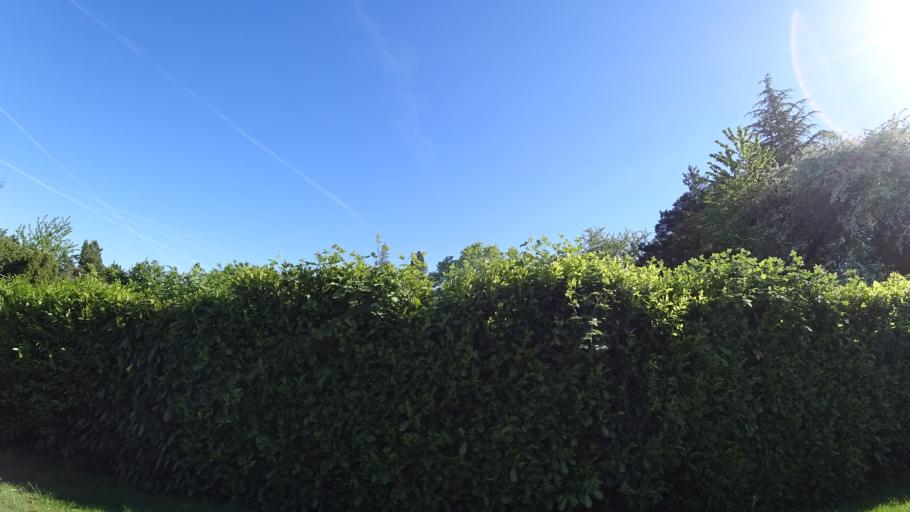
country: US
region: Oregon
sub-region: Washington County
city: Raleigh Hills
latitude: 45.4876
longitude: -122.7494
